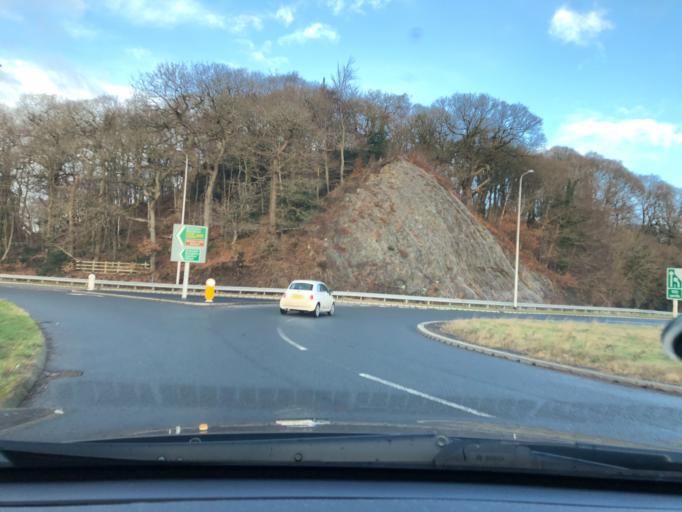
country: GB
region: England
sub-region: Cumbria
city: Ulverston
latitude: 54.2350
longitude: -3.0505
